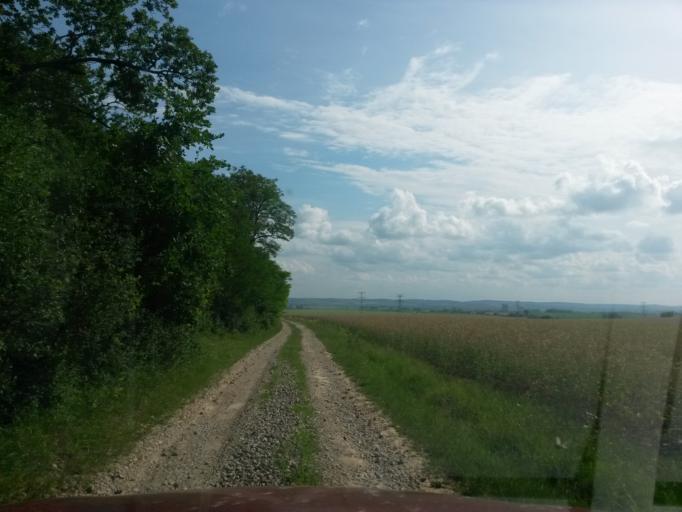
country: SK
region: Kosicky
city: Moldava nad Bodvou
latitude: 48.6150
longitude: 21.1037
